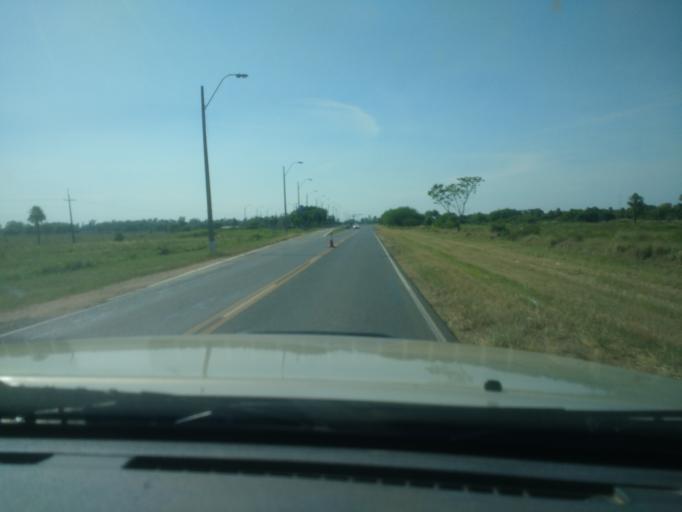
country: PY
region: Presidente Hayes
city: Benjamin Aceval
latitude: -24.9321
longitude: -57.5628
